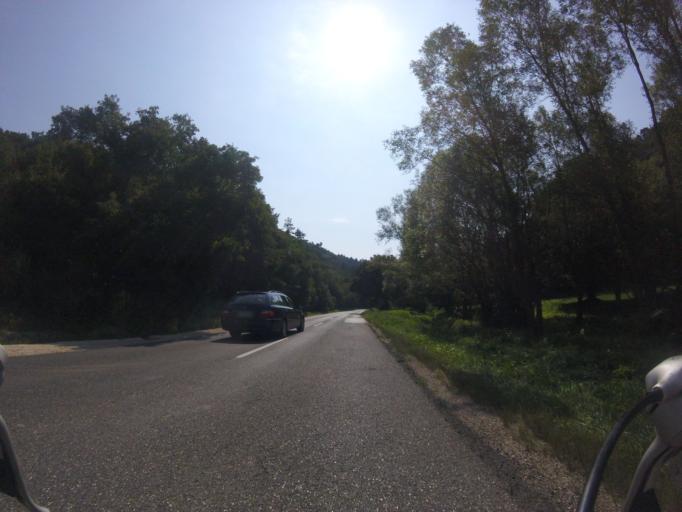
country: HU
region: Veszprem
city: Csopak
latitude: 46.9854
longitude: 17.9197
